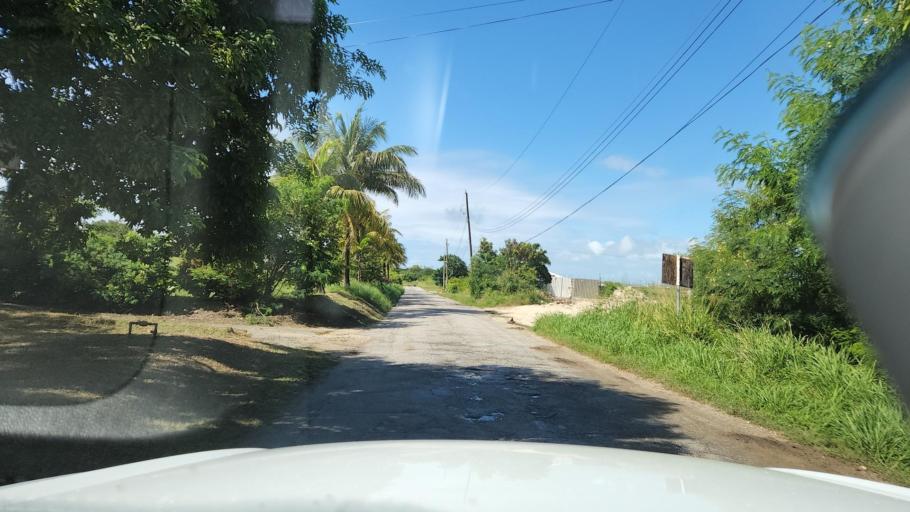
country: BB
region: Christ Church
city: Oistins
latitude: 13.1037
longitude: -59.5111
